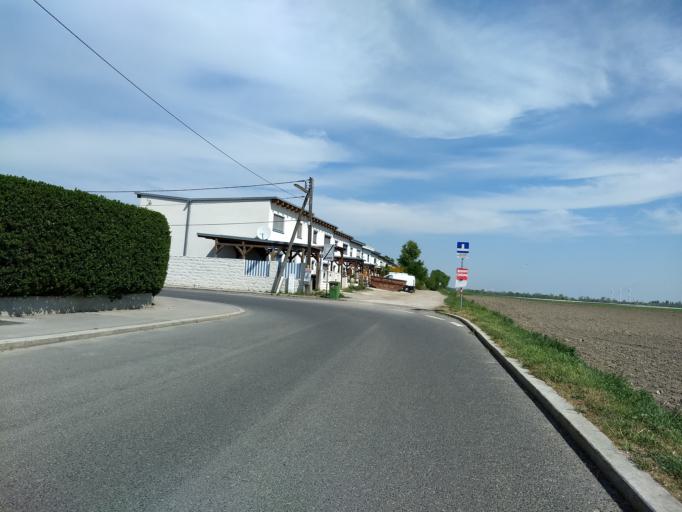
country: AT
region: Lower Austria
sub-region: Politischer Bezirk Ganserndorf
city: Aderklaa
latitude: 48.2396
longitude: 16.5048
